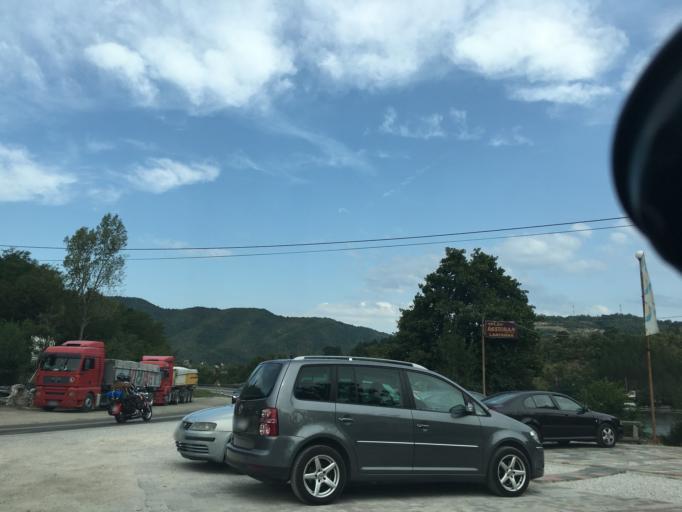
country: RS
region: Central Serbia
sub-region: Moravicki Okrug
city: Lucani
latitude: 43.9131
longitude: 20.2352
